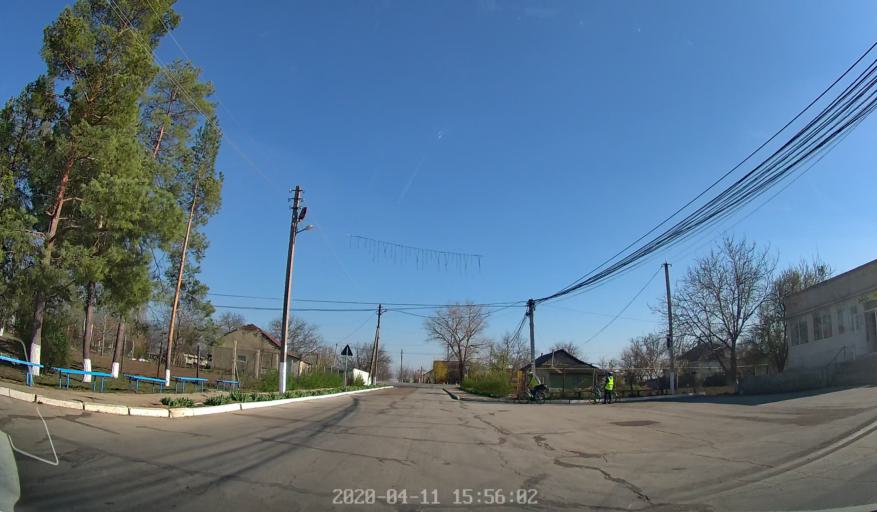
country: MD
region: Chisinau
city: Vadul lui Voda
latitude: 47.0939
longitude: 29.1782
